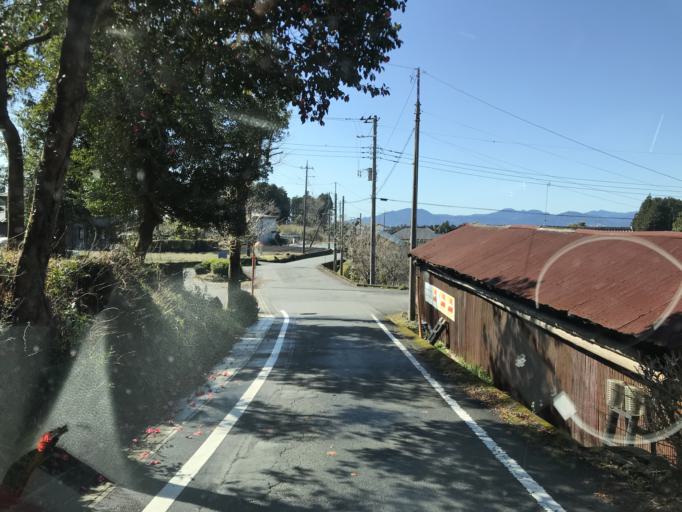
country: JP
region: Shizuoka
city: Fujinomiya
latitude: 35.2539
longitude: 138.6645
